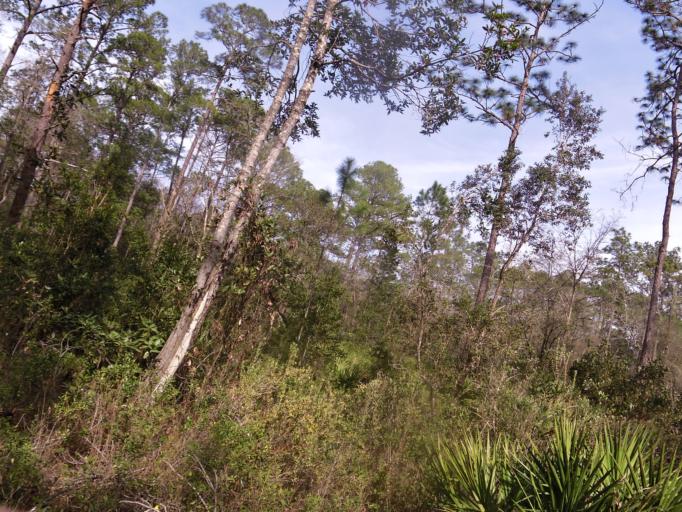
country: US
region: Florida
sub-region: Clay County
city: Middleburg
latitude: 30.1190
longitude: -81.9065
